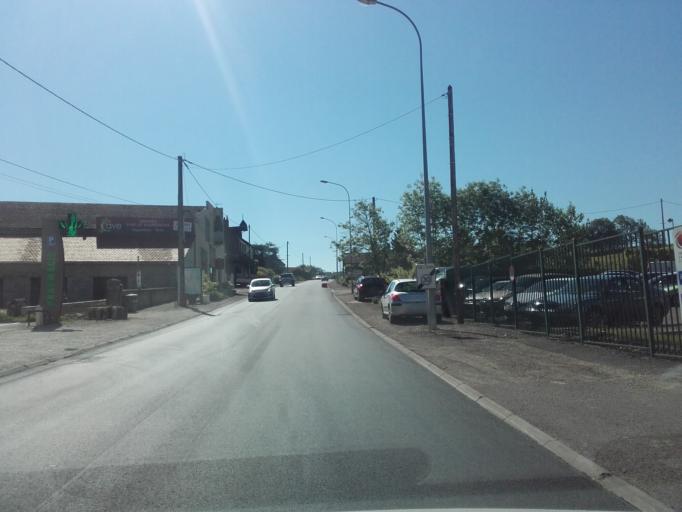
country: FR
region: Bourgogne
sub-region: Departement de la Cote-d'Or
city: Nolay
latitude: 46.9494
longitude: 4.6393
